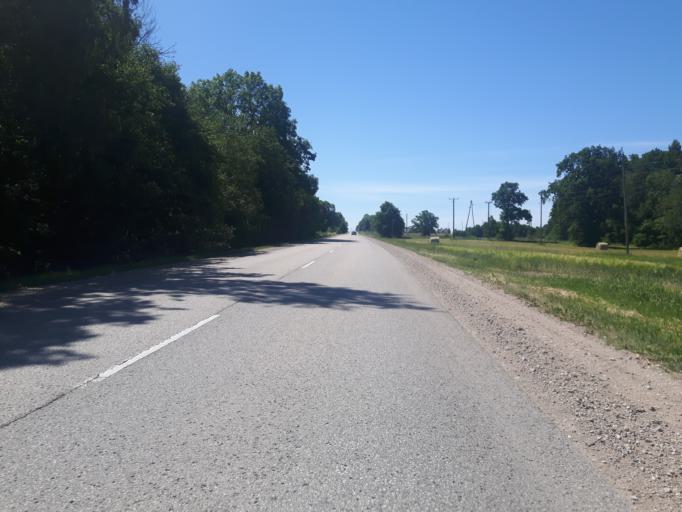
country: LV
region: Durbe
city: Liegi
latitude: 56.5934
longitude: 21.2743
